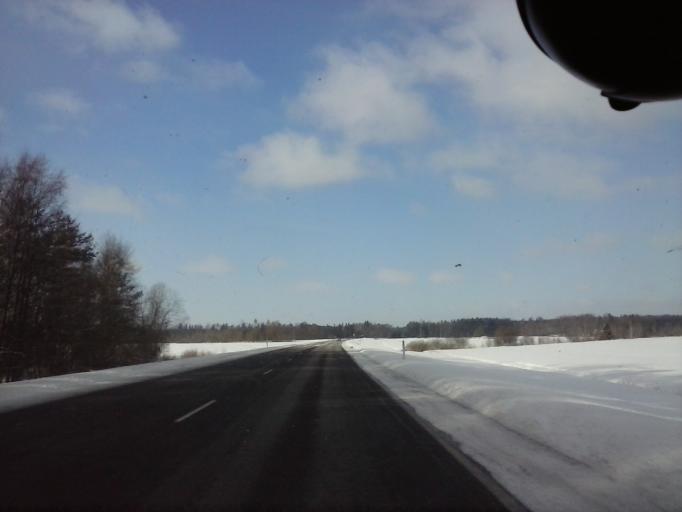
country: EE
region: Paernumaa
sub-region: Paikuse vald
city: Paikuse
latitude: 58.2714
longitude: 24.6343
